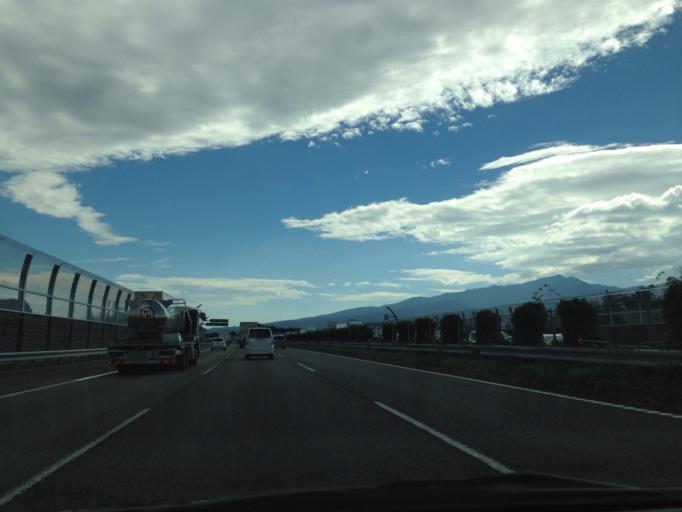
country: JP
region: Shizuoka
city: Gotemba
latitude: 35.2796
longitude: 138.9208
